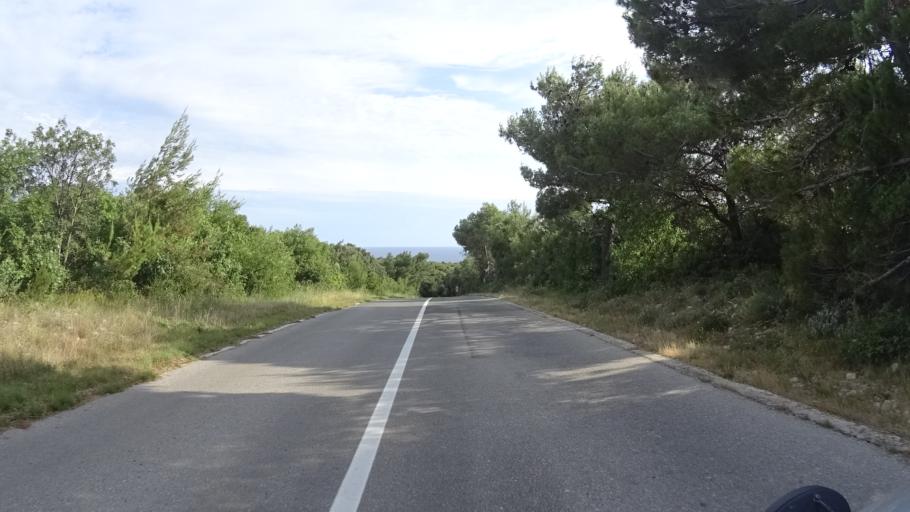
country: HR
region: Istarska
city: Rasa
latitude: 44.9768
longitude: 14.1058
